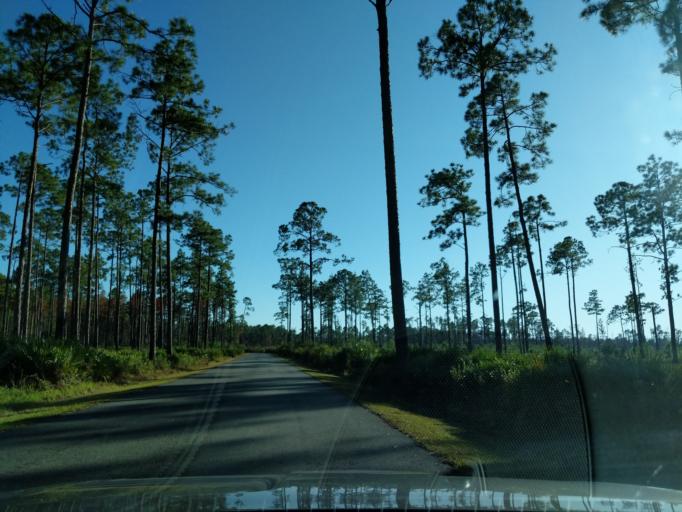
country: US
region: Georgia
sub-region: Charlton County
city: Folkston
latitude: 30.7245
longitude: -82.1399
